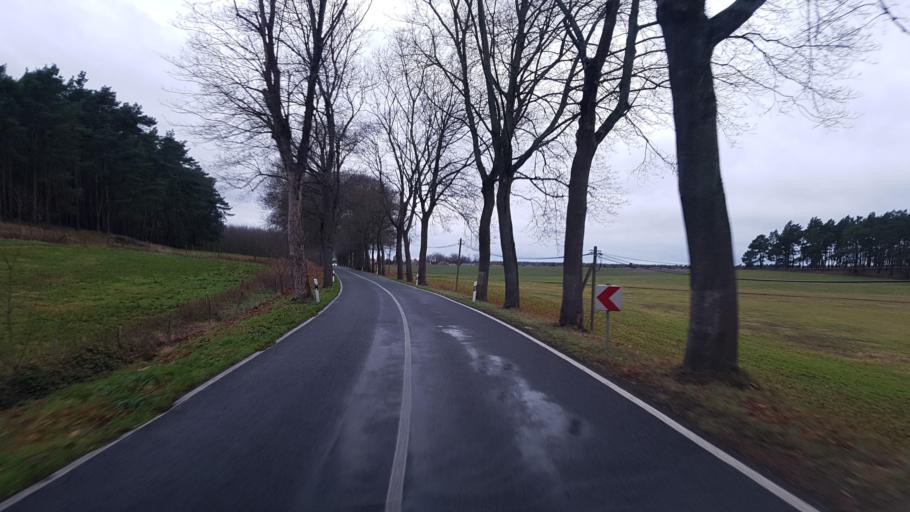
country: DE
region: Brandenburg
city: Tauche
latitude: 52.0755
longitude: 14.0697
